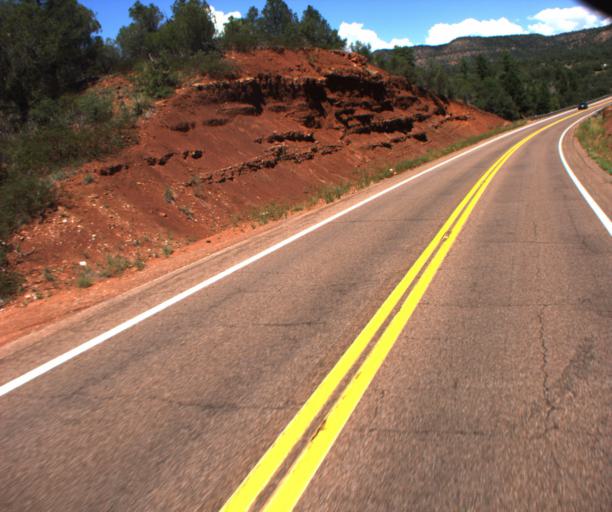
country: US
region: Arizona
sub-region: Navajo County
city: Cibecue
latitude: 33.9524
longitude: -110.3318
